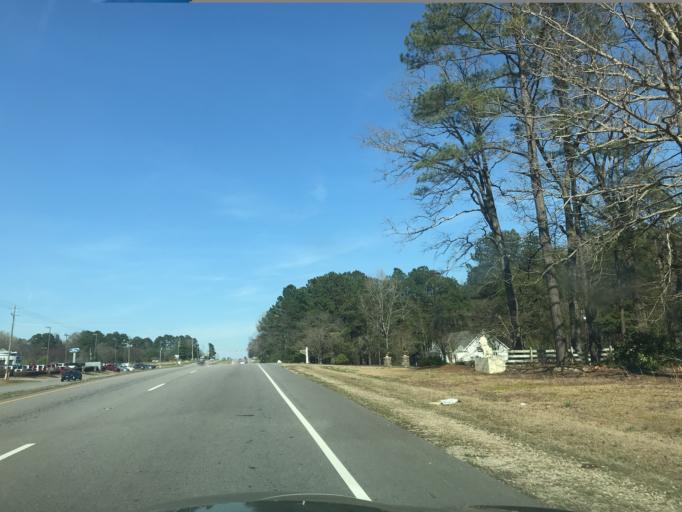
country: US
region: North Carolina
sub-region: Wake County
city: Fuquay-Varina
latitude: 35.6220
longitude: -78.7271
